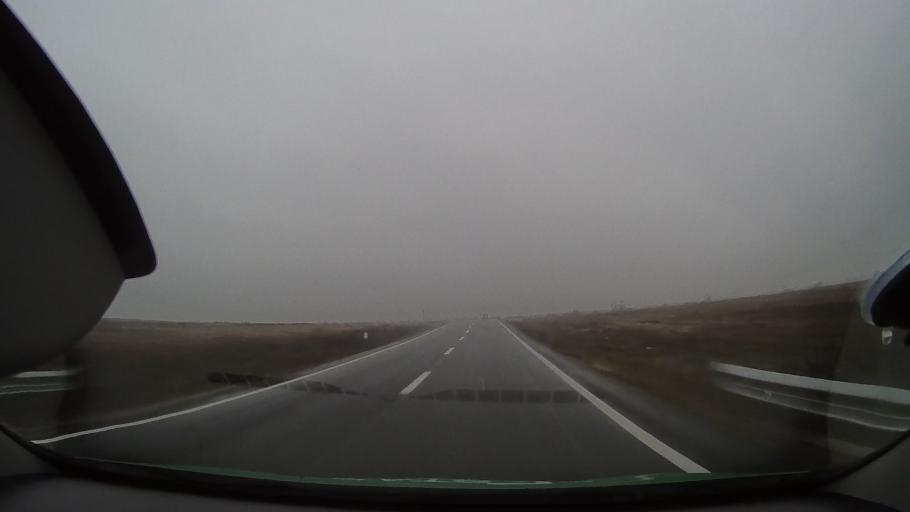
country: RO
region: Arad
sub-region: Comuna Craiova
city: Craiova
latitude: 46.6263
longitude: 21.9583
